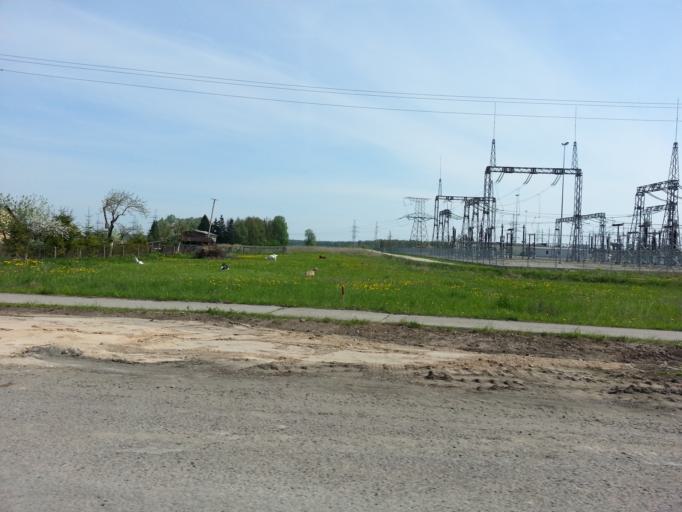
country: LT
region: Panevezys
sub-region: Panevezys City
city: Panevezys
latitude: 55.7626
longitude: 24.3024
